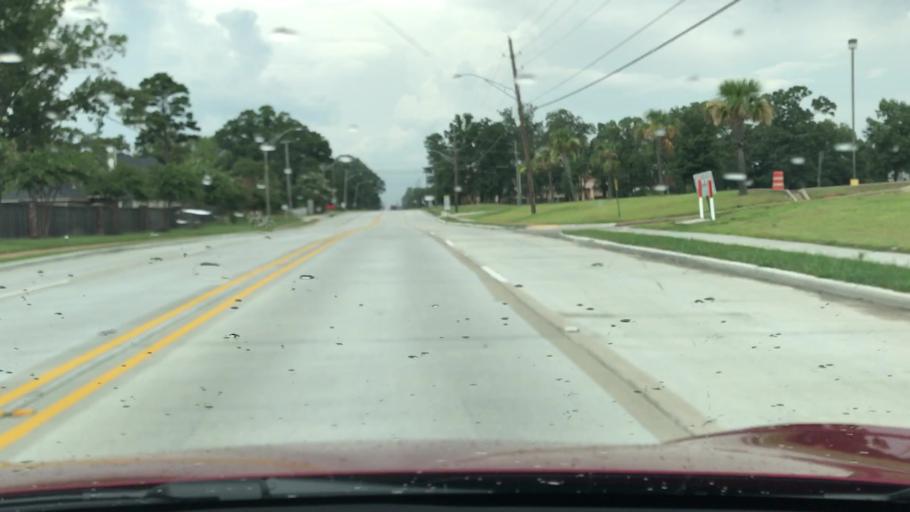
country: US
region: Louisiana
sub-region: Bossier Parish
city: Bossier City
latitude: 32.4045
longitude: -93.7633
